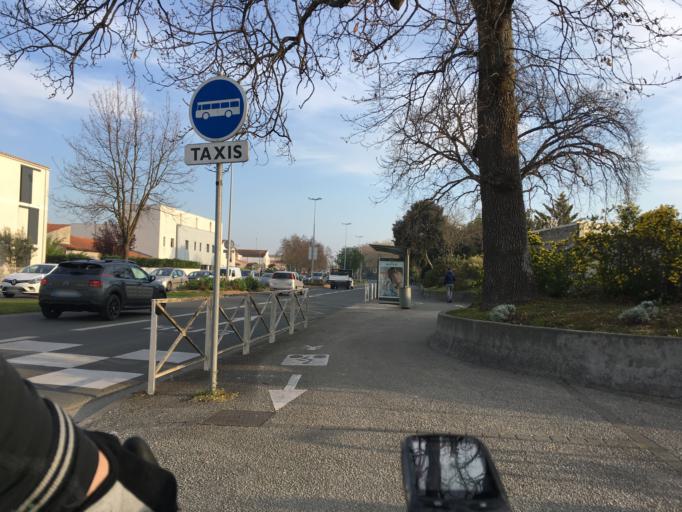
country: FR
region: Poitou-Charentes
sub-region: Departement de la Charente-Maritime
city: La Rochelle
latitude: 46.1735
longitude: -1.1503
